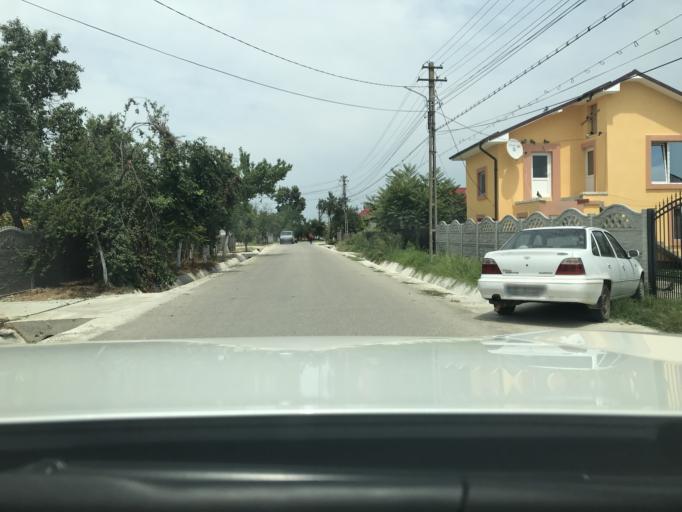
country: RO
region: Olt
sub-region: Comuna Osica de Sus
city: Osica de Sus
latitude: 44.2557
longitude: 24.3153
